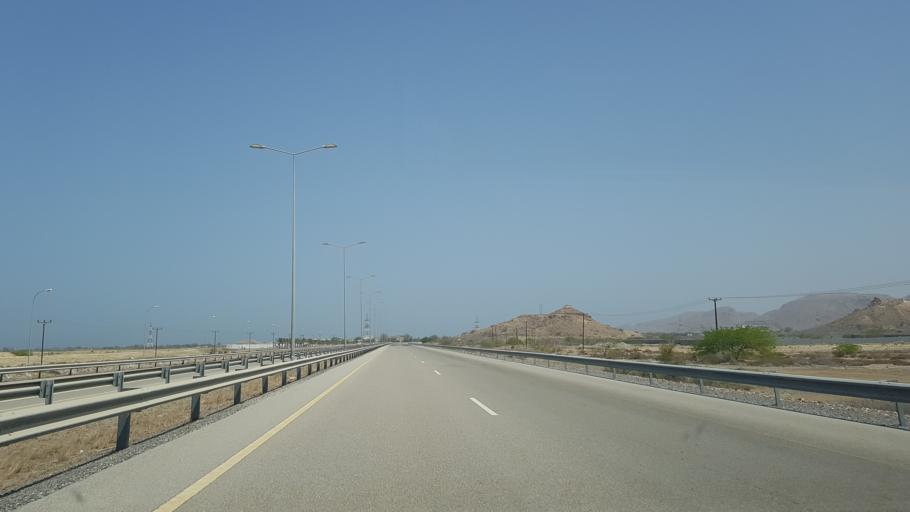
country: OM
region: Muhafazat Masqat
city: Muscat
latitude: 23.2113
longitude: 58.9404
